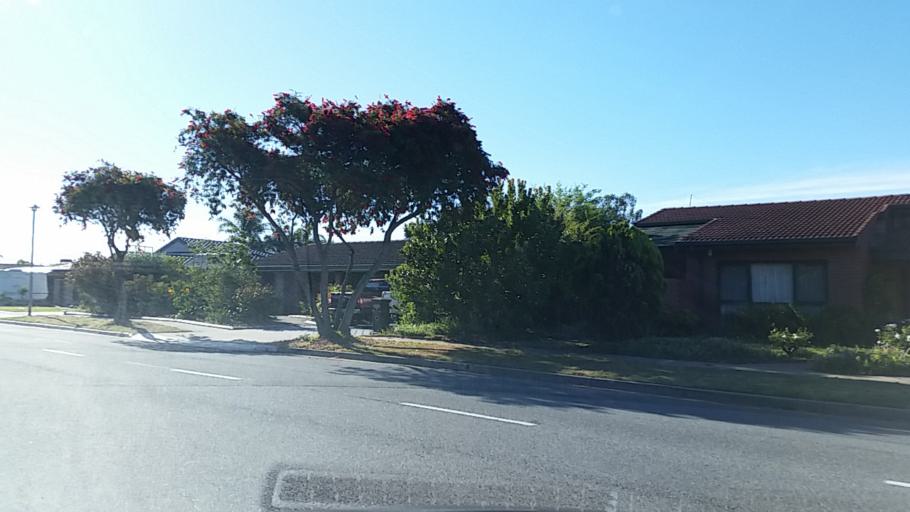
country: AU
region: South Australia
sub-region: Charles Sturt
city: West Lakes Shore
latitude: -34.8680
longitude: 138.4979
